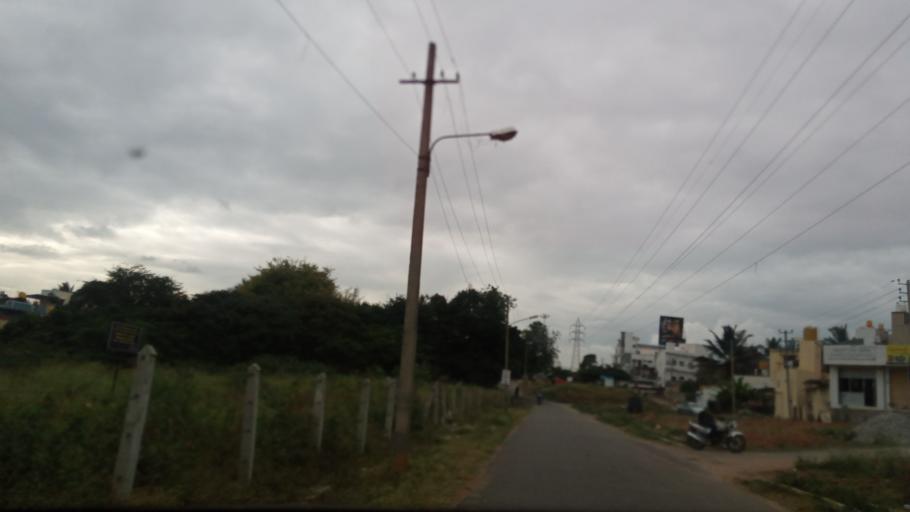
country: IN
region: Karnataka
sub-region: Mysore
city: Mysore
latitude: 12.2940
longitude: 76.6154
